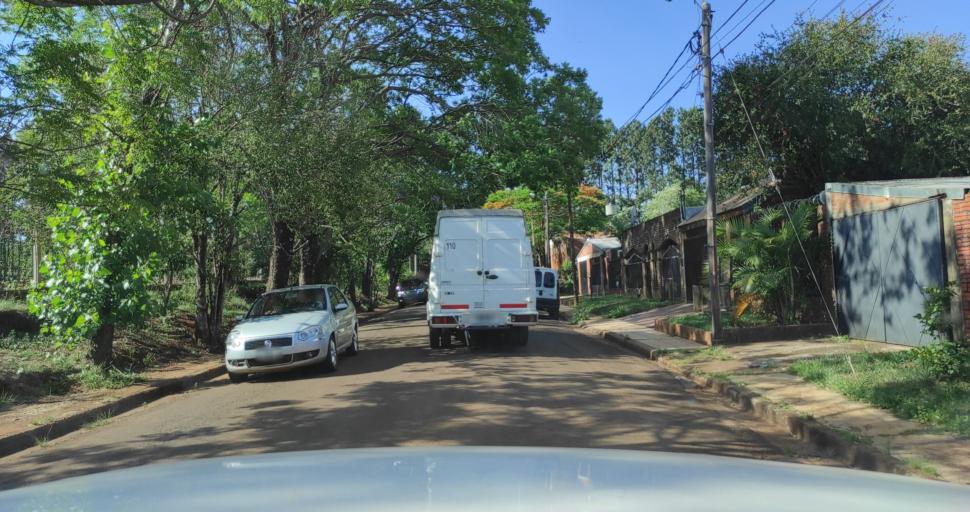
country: AR
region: Misiones
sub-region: Departamento de Capital
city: Posadas
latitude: -27.4121
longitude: -55.9222
